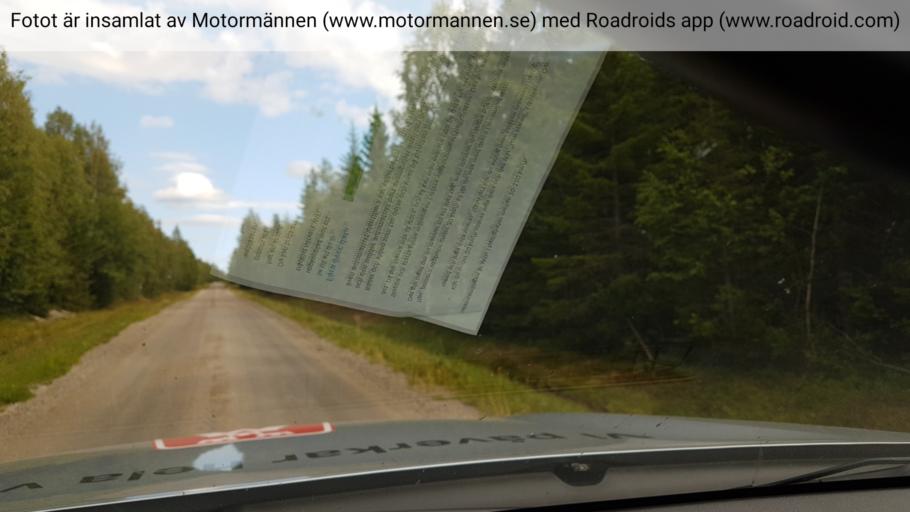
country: SE
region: Vaesterbotten
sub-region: Skelleftea Kommun
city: Storvik
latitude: 65.2144
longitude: 20.8429
